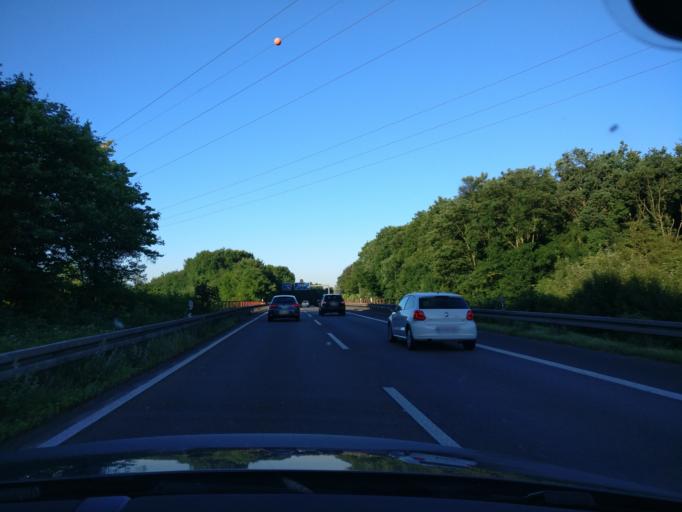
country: DE
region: North Rhine-Westphalia
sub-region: Regierungsbezirk Dusseldorf
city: Ratingen
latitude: 51.2937
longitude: 6.8031
